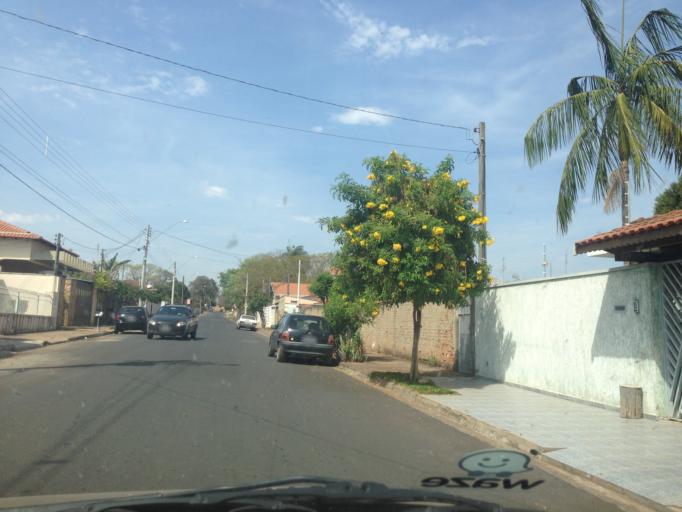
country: BR
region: Sao Paulo
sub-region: Casa Branca
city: Casa Branca
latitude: -21.7803
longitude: -47.0833
